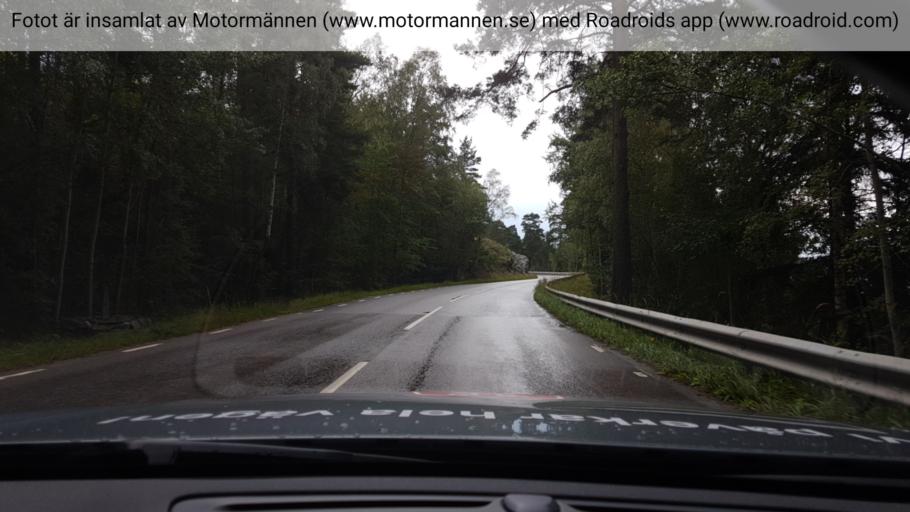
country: SE
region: Uppsala
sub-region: Habo Kommun
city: Balsta
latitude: 59.5489
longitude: 17.5589
